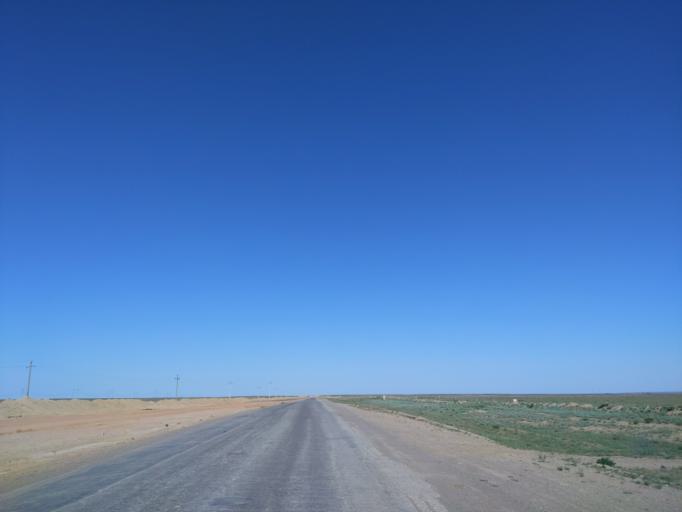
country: KZ
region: Almaty Oblysy
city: Bakanas
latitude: 44.1511
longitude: 75.8621
